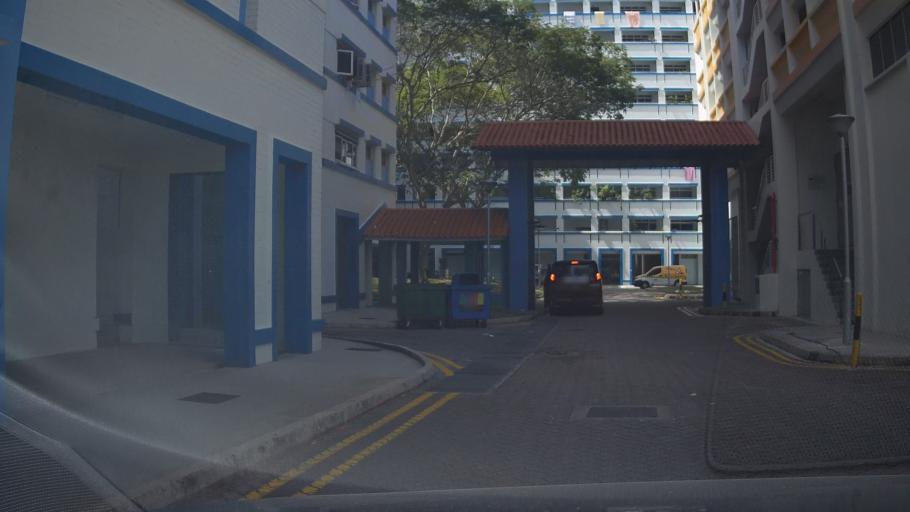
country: SG
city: Singapore
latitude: 1.3643
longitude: 103.9605
